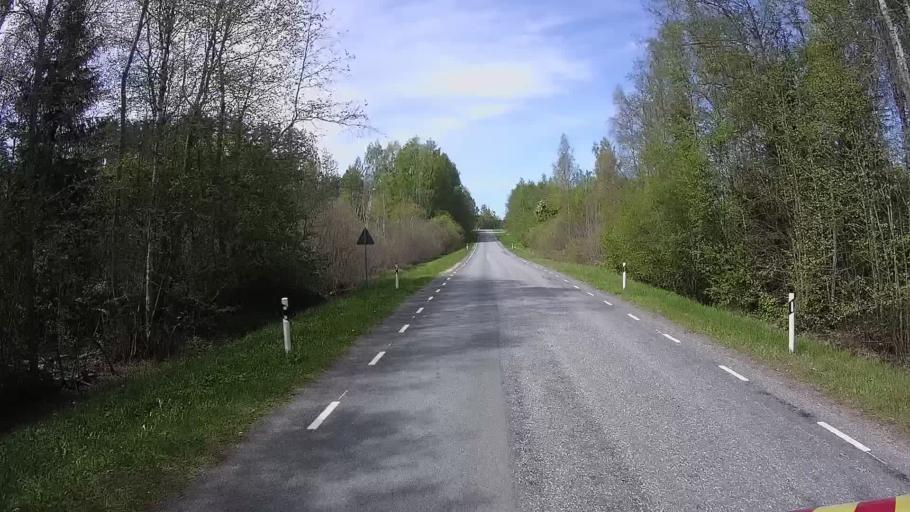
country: EE
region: Valgamaa
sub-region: Valga linn
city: Valga
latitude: 57.6550
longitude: 26.2945
